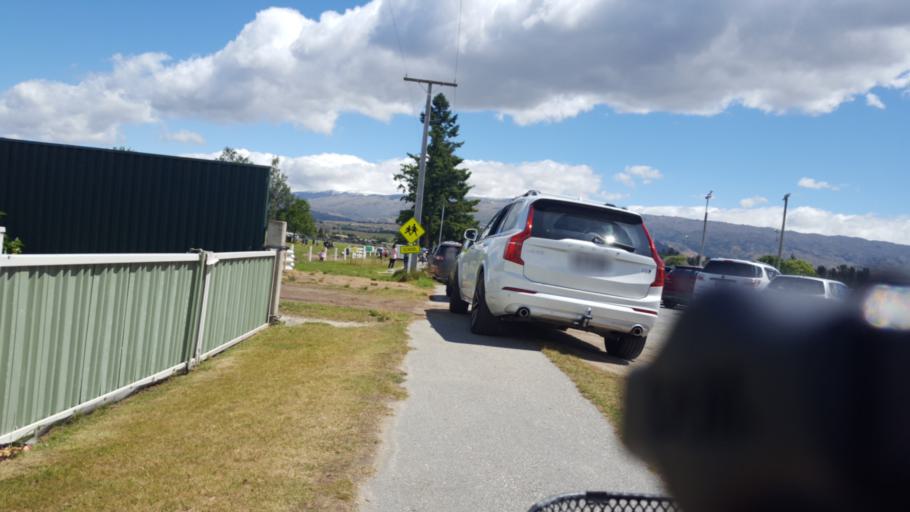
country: NZ
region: Otago
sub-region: Queenstown-Lakes District
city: Wanaka
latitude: -45.2419
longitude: 169.3883
